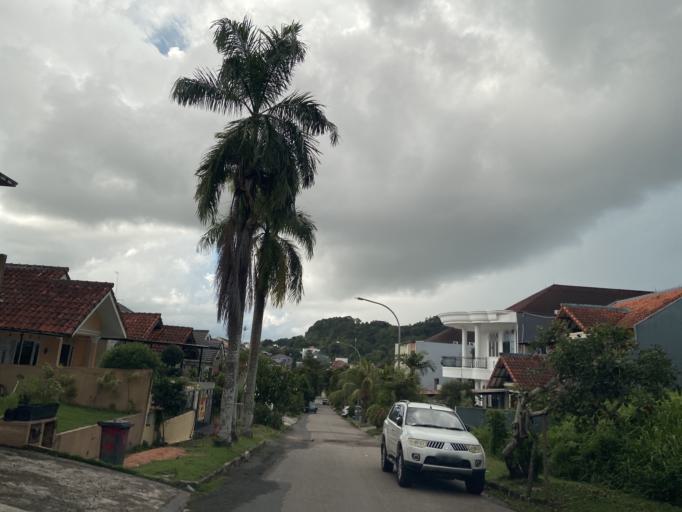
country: SG
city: Singapore
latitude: 1.1055
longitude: 104.0240
